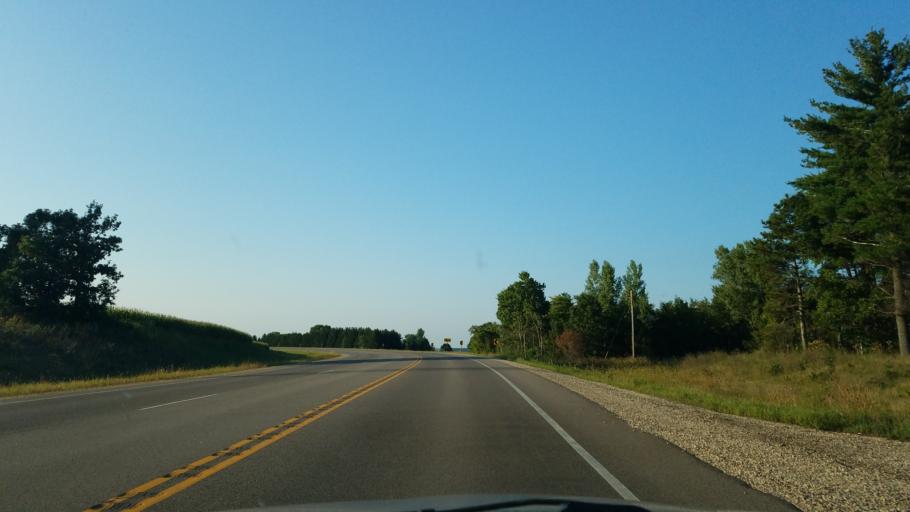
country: US
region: Wisconsin
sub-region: Saint Croix County
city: Baldwin
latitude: 45.1143
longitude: -92.3755
